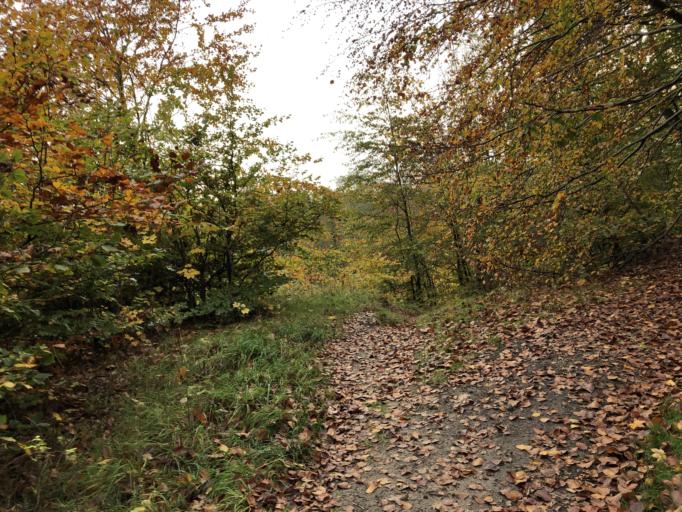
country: DK
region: Capital Region
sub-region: Lyngby-Tarbaek Kommune
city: Kongens Lyngby
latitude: 55.8011
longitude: 12.5049
